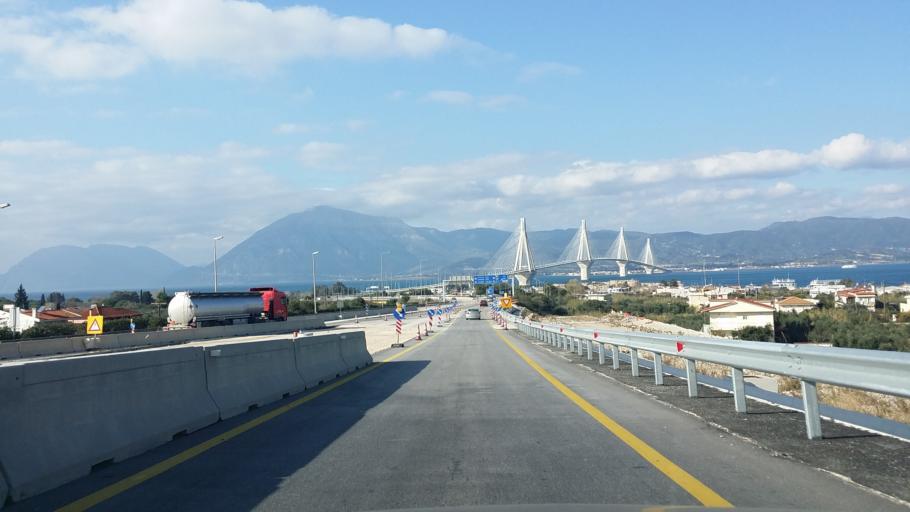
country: GR
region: West Greece
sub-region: Nomos Achaias
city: Rio
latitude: 38.3014
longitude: 21.7901
